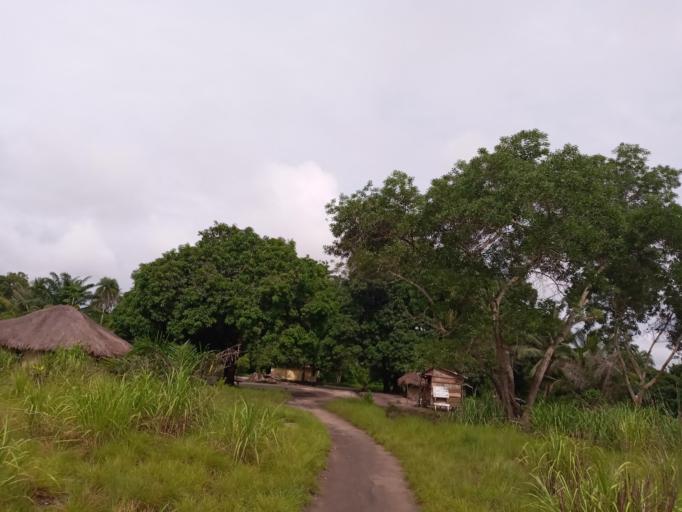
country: SL
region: Southern Province
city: Bonthe
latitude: 7.5198
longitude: -12.5377
